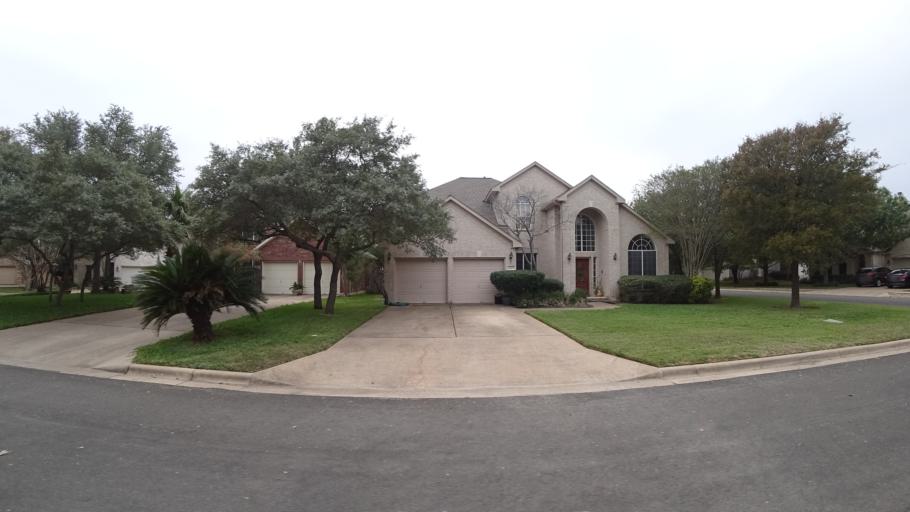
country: US
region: Texas
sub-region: Travis County
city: Shady Hollow
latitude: 30.1853
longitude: -97.8873
